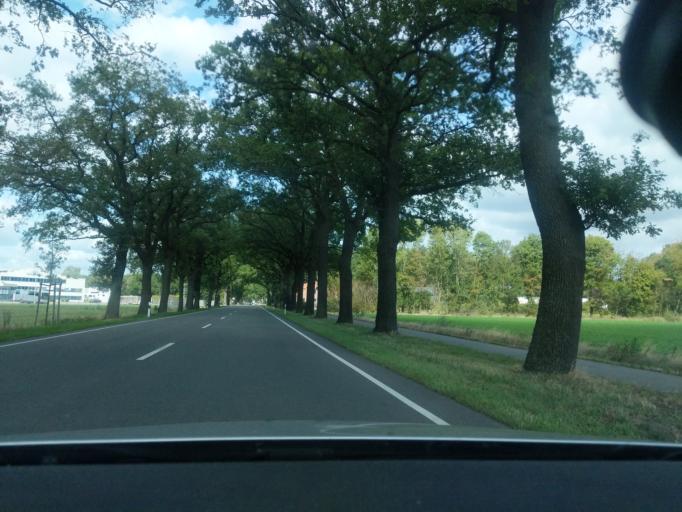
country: DE
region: Lower Saxony
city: Bohmte
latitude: 52.3846
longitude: 8.3108
